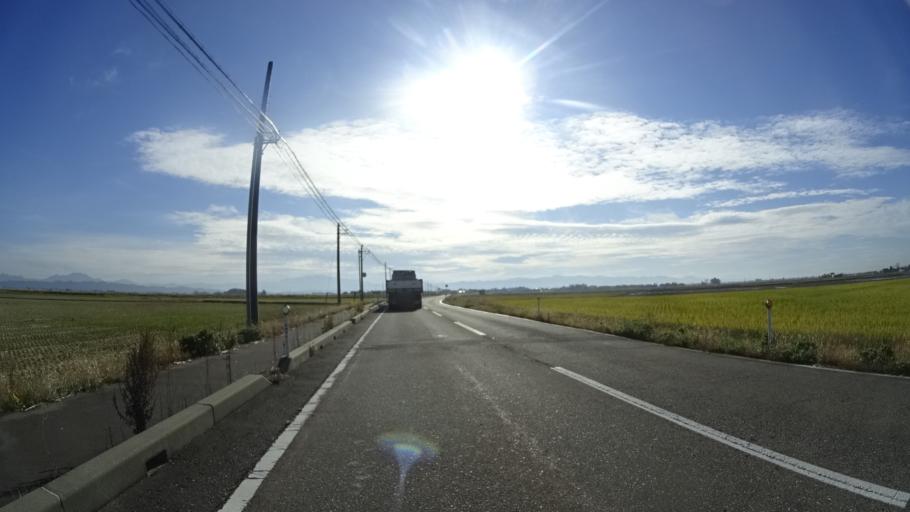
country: JP
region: Niigata
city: Mitsuke
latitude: 37.5675
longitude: 138.8446
